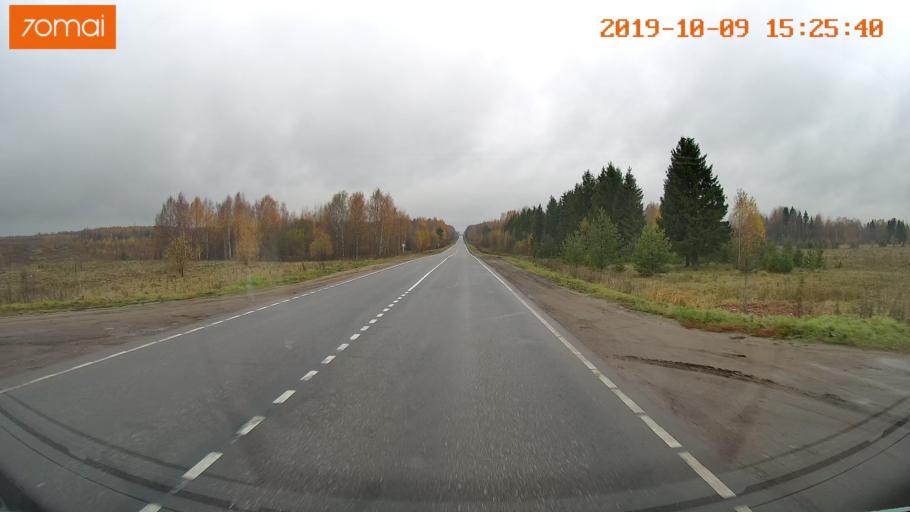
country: RU
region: Kostroma
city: Susanino
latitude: 58.0254
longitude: 41.4227
